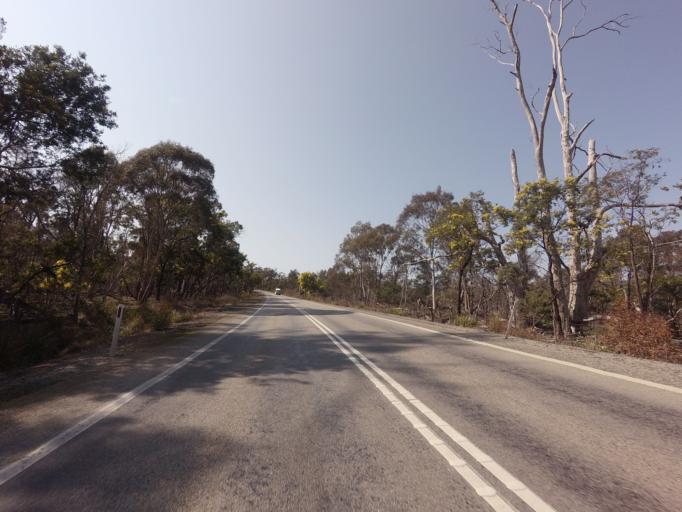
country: AU
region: Tasmania
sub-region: Northern Midlands
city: Evandale
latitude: -41.8282
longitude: 147.5015
